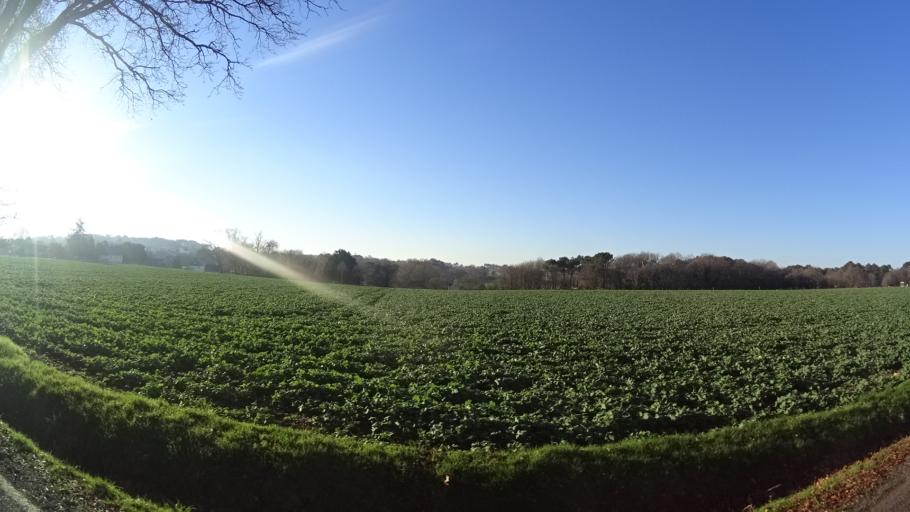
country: FR
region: Brittany
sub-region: Departement du Morbihan
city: Allaire
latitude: 47.6542
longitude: -2.1507
